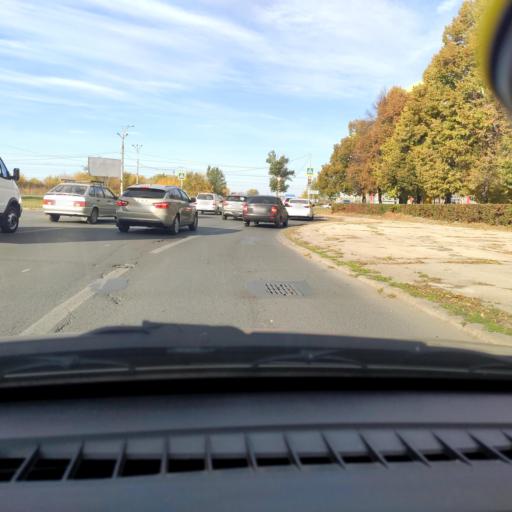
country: RU
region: Samara
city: Tol'yatti
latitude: 53.5167
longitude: 49.2599
